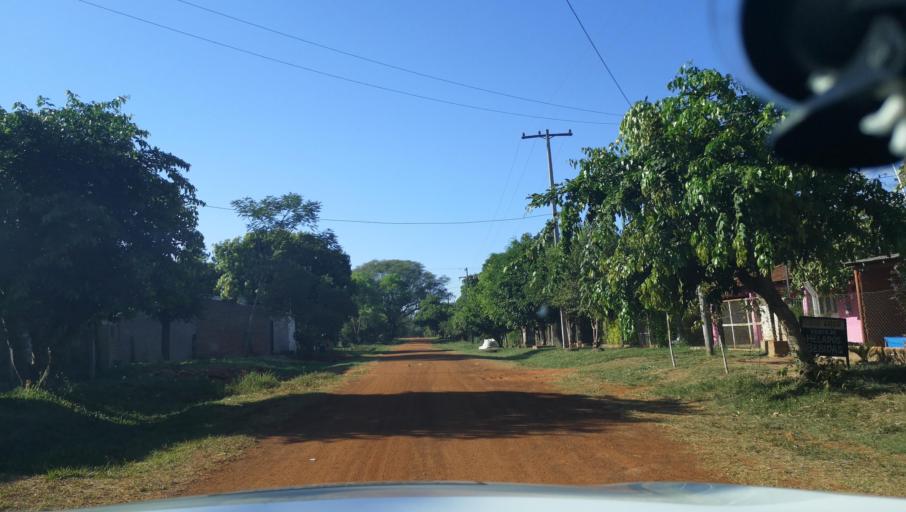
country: PY
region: Itapua
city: Carmen del Parana
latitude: -27.1691
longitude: -56.2407
